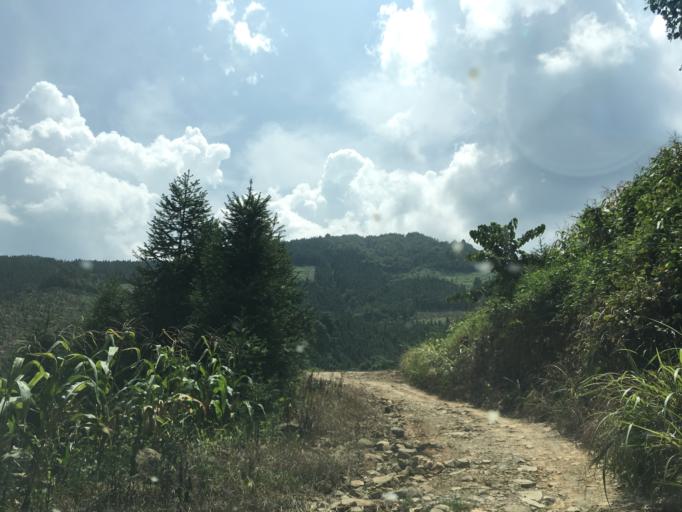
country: CN
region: Guangxi Zhuangzu Zizhiqu
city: Xinzhou
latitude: 24.9546
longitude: 105.7856
